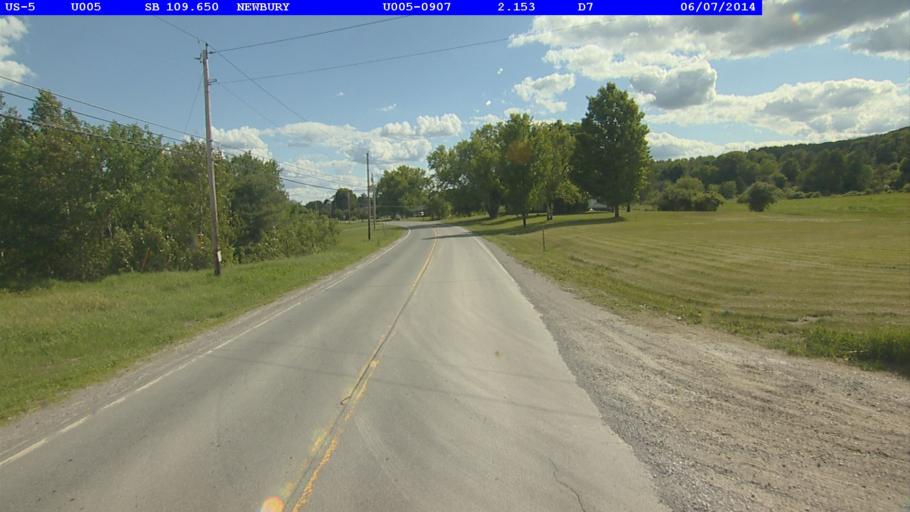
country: US
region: New Hampshire
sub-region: Grafton County
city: Haverhill
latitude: 44.0596
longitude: -72.0705
